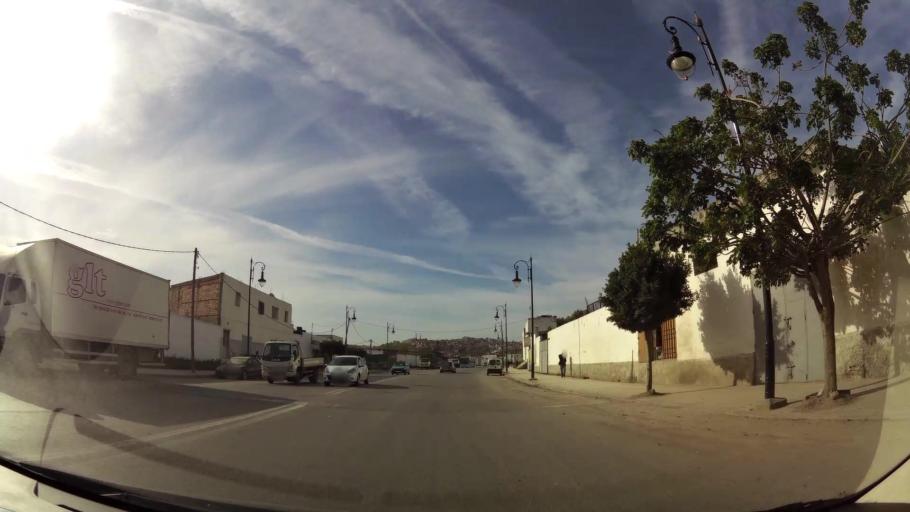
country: MA
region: Tanger-Tetouan
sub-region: Tanger-Assilah
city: Tangier
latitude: 35.7641
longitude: -5.7831
